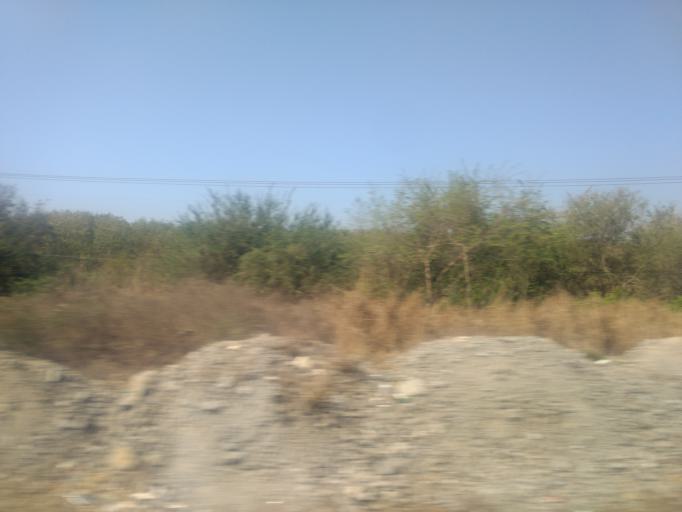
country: MX
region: Colima
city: El Colomo
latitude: 19.0497
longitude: -104.2666
